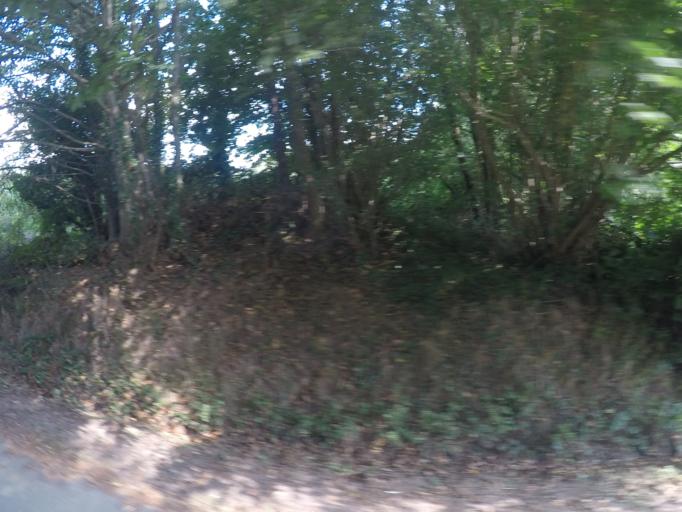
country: FR
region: Brittany
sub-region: Departement des Cotes-d'Armor
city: Saint-Donan
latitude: 48.5016
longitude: -2.9132
